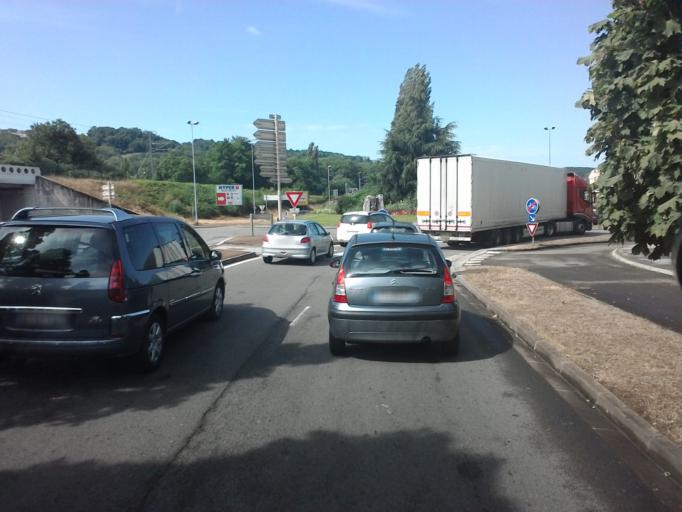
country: FR
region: Franche-Comte
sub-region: Departement du Jura
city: Perrigny
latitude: 46.6706
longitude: 5.5725
